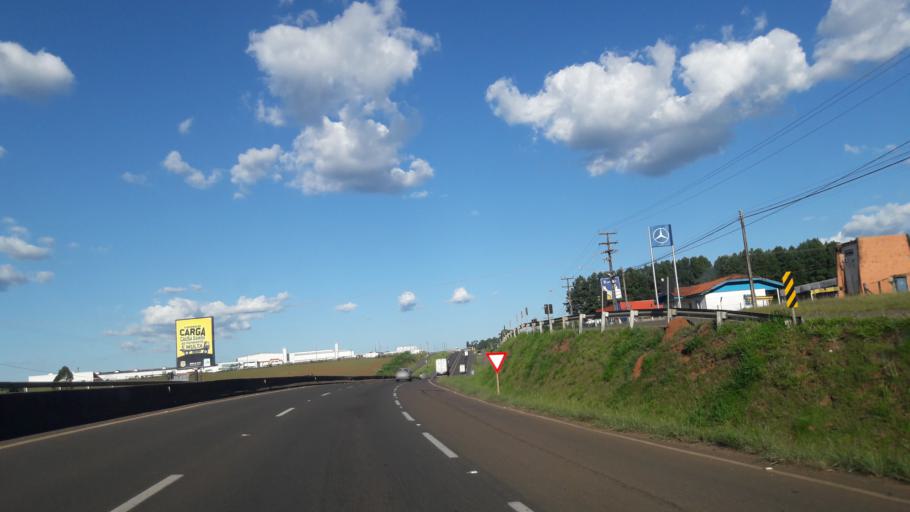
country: BR
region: Parana
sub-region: Guarapuava
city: Guarapuava
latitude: -25.3485
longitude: -51.4547
